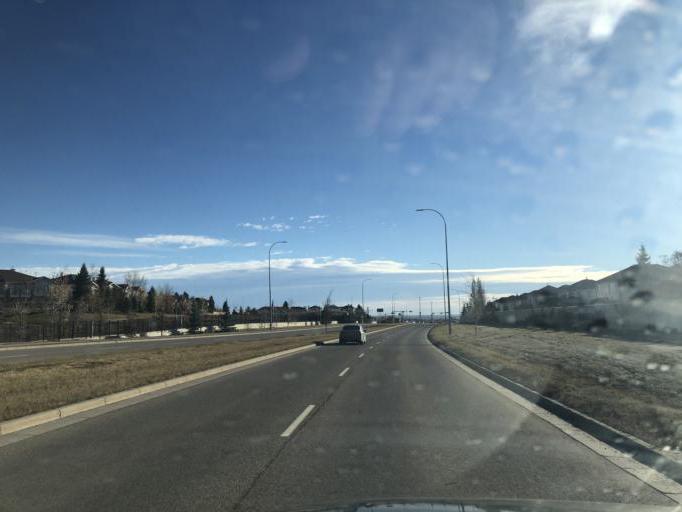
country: CA
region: Alberta
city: Calgary
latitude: 51.0376
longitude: -114.1830
